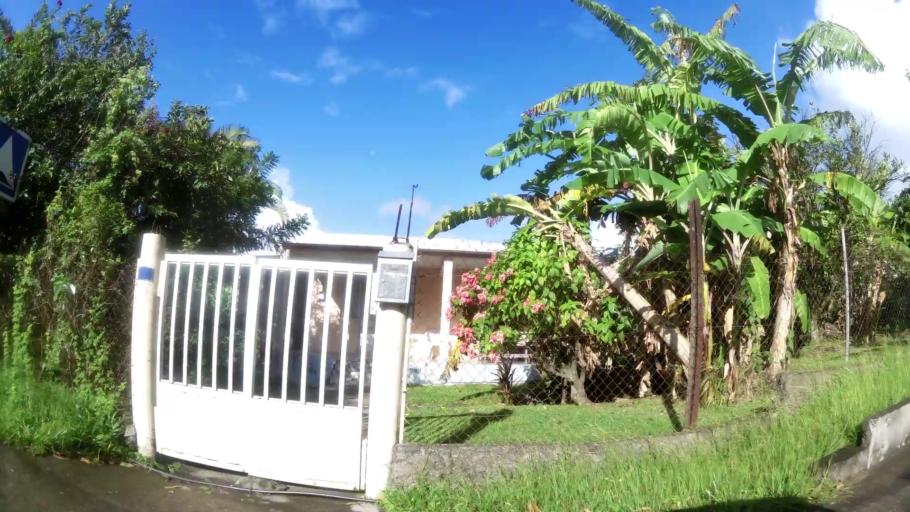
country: MQ
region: Martinique
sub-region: Martinique
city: Ducos
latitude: 14.5715
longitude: -60.9653
